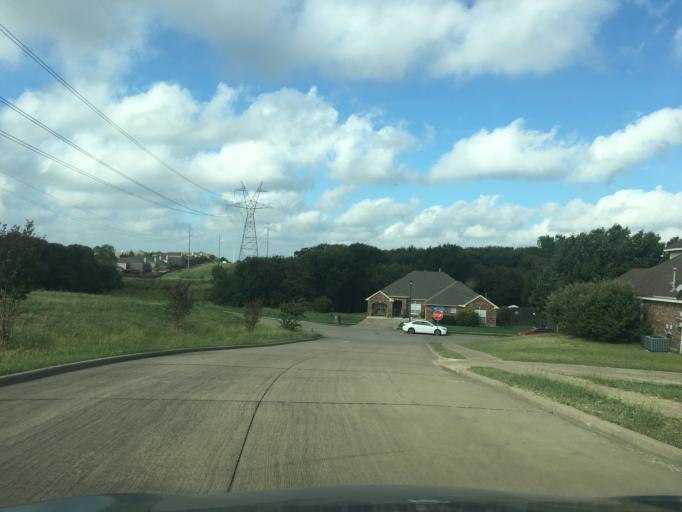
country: US
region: Texas
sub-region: Dallas County
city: Sachse
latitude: 32.9648
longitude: -96.5924
